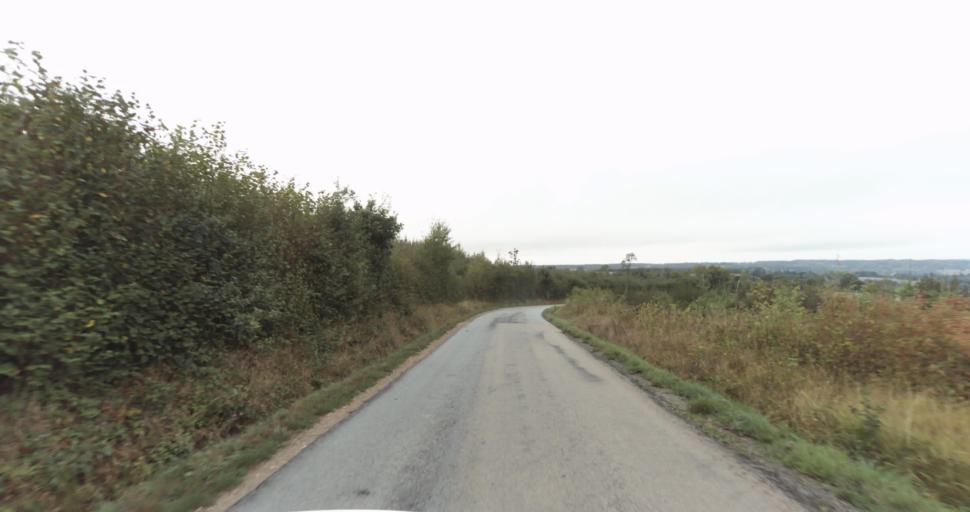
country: FR
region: Lower Normandy
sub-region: Departement de l'Orne
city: Trun
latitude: 48.9044
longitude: 0.1045
